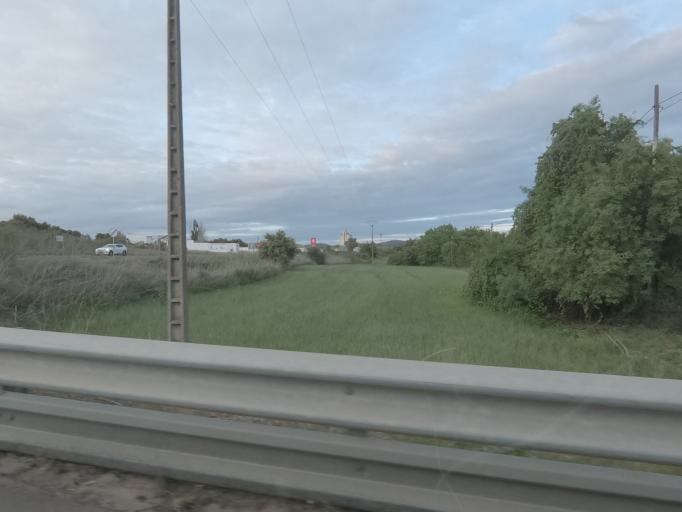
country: ES
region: Extremadura
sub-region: Provincia de Badajoz
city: La Roca de la Sierra
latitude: 39.1141
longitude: -6.6866
